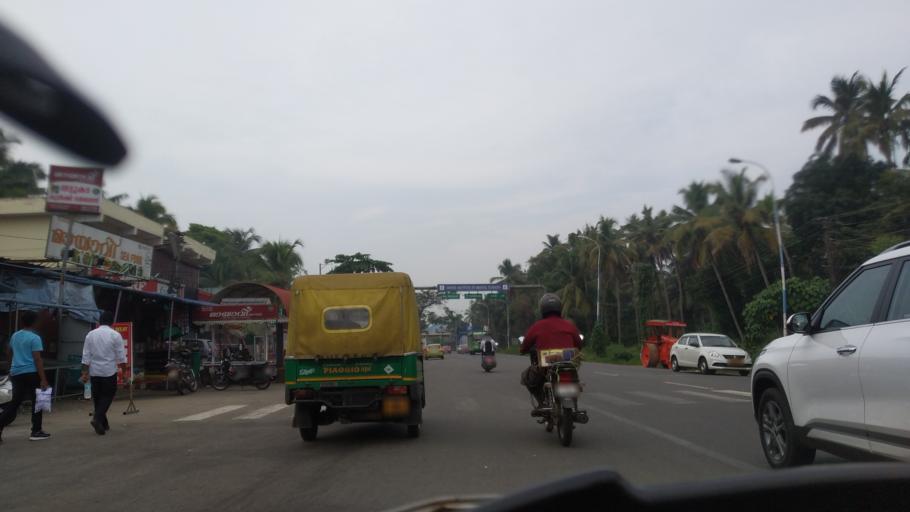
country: IN
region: Kerala
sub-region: Ernakulam
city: Elur
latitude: 10.0435
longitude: 76.2987
